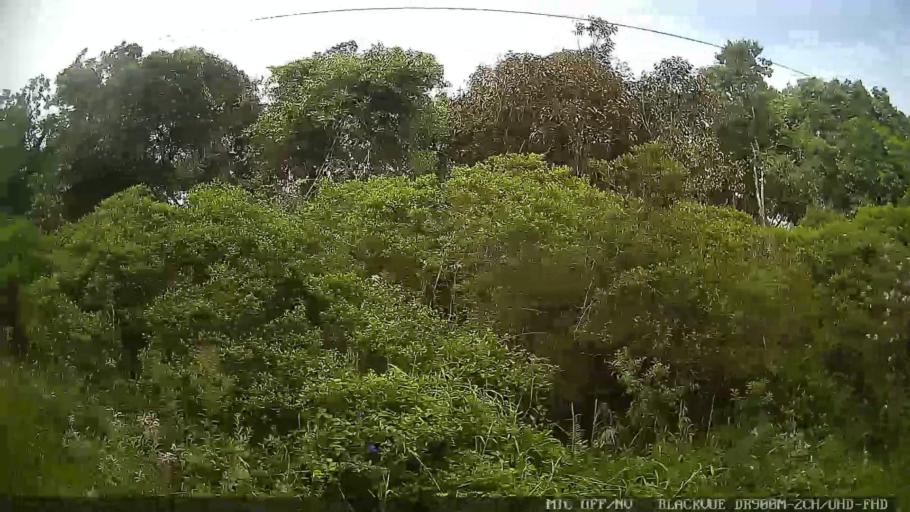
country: BR
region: Sao Paulo
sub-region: Peruibe
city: Peruibe
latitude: -24.2209
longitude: -46.9262
